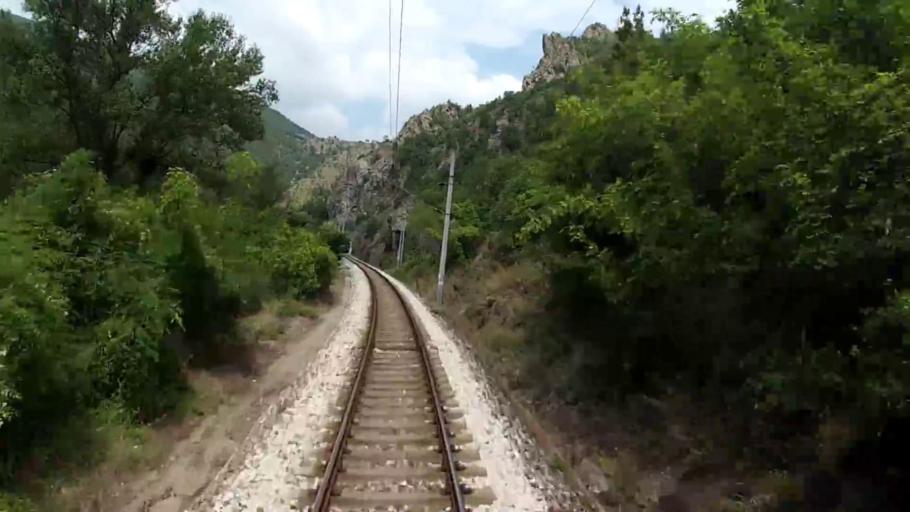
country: BG
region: Blagoevgrad
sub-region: Obshtina Kresna
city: Stara Kresna
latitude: 41.8272
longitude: 23.1535
